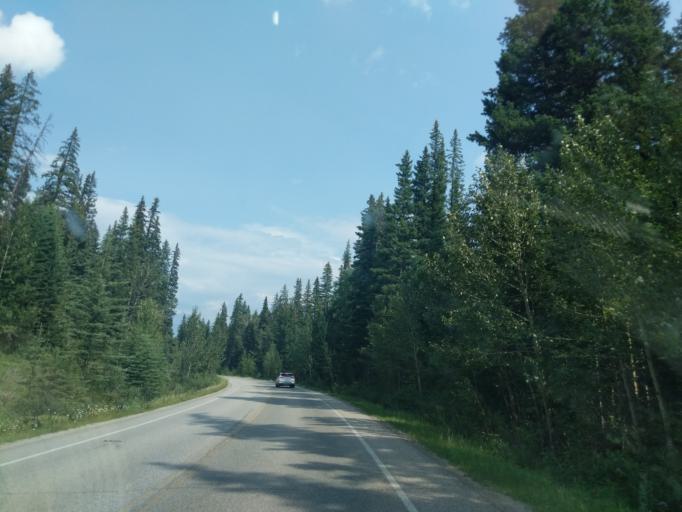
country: CA
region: Alberta
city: Banff
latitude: 51.1679
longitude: -115.6764
